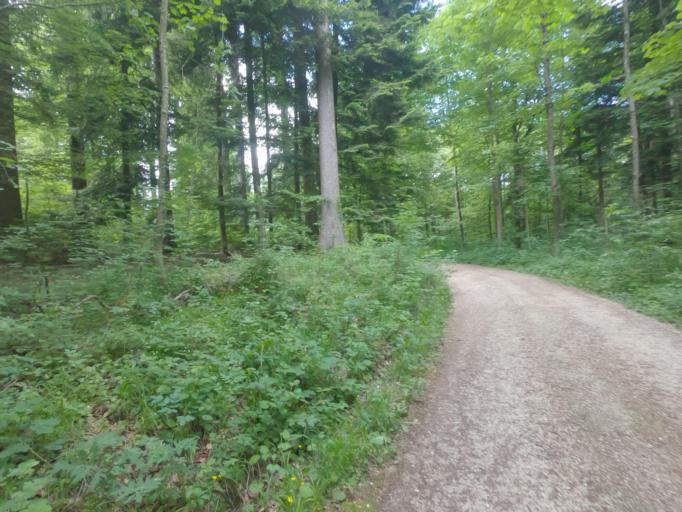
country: CH
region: Solothurn
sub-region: Bezirk Lebern
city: Riedholz
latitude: 47.2393
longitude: 7.5724
